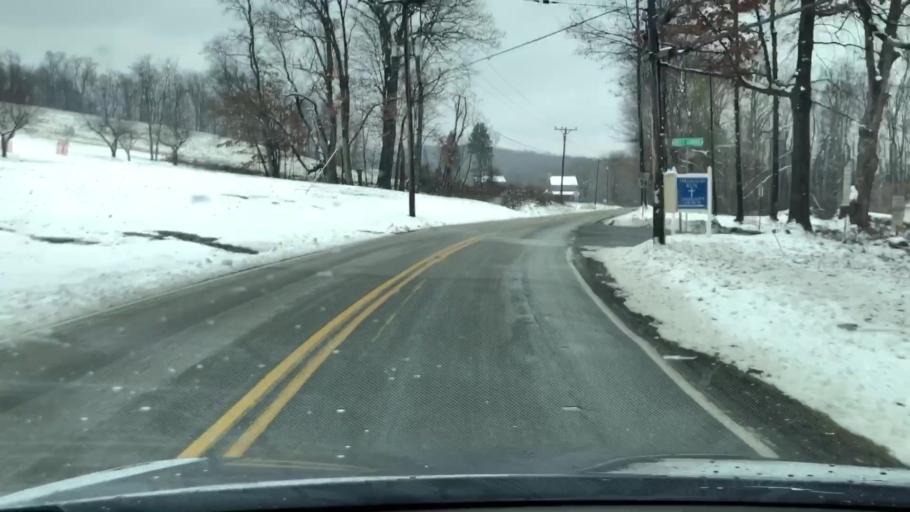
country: US
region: Pennsylvania
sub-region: Fayette County
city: Dunbar
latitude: 39.8421
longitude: -79.5212
